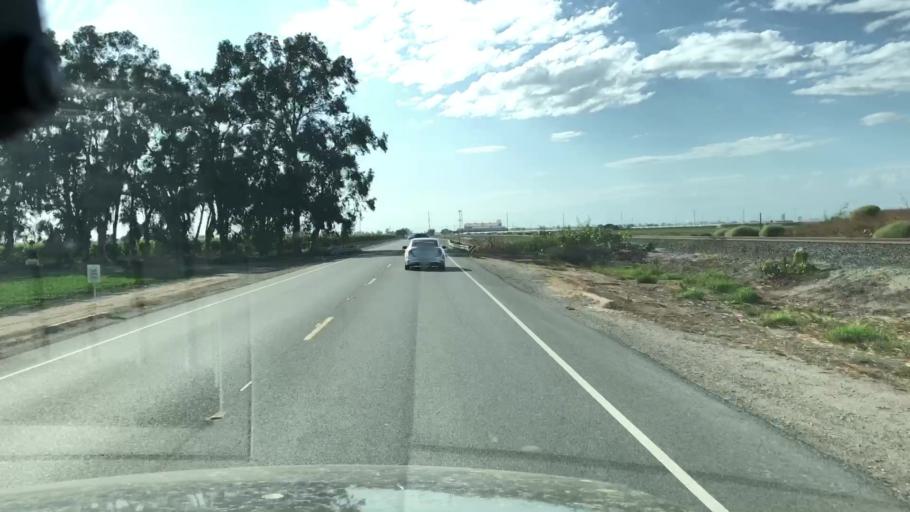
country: US
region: California
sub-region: Ventura County
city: Camarillo
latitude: 34.1965
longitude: -119.0864
